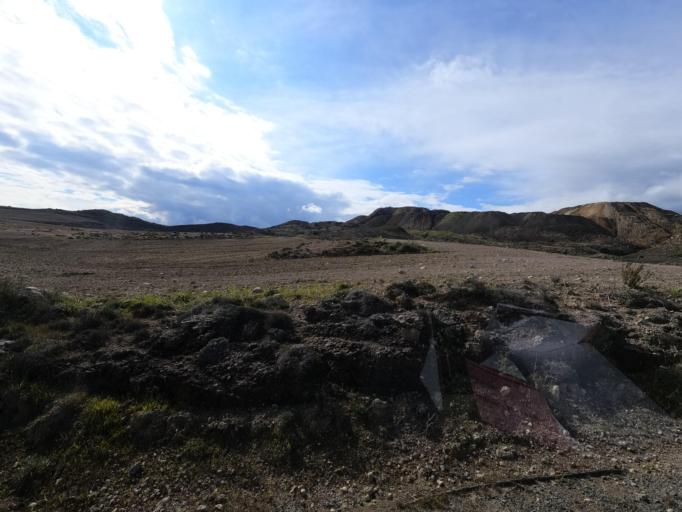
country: CY
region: Lefkosia
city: Lefka
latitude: 35.1063
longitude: 32.8935
